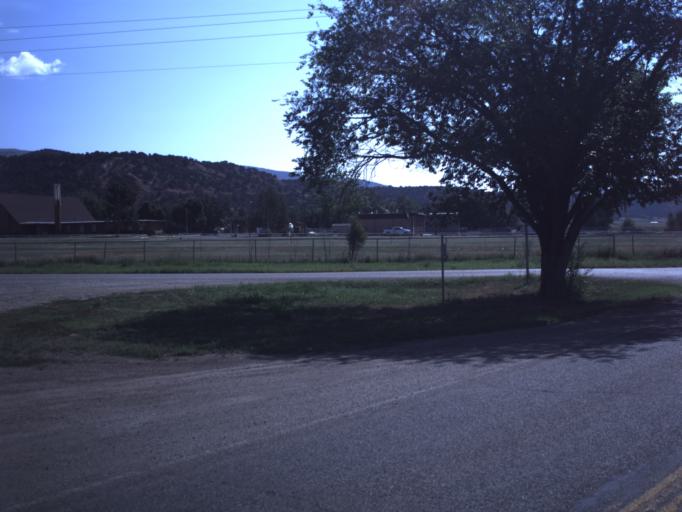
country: US
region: Utah
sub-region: Duchesne County
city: Duchesne
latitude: 40.3514
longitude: -110.7093
